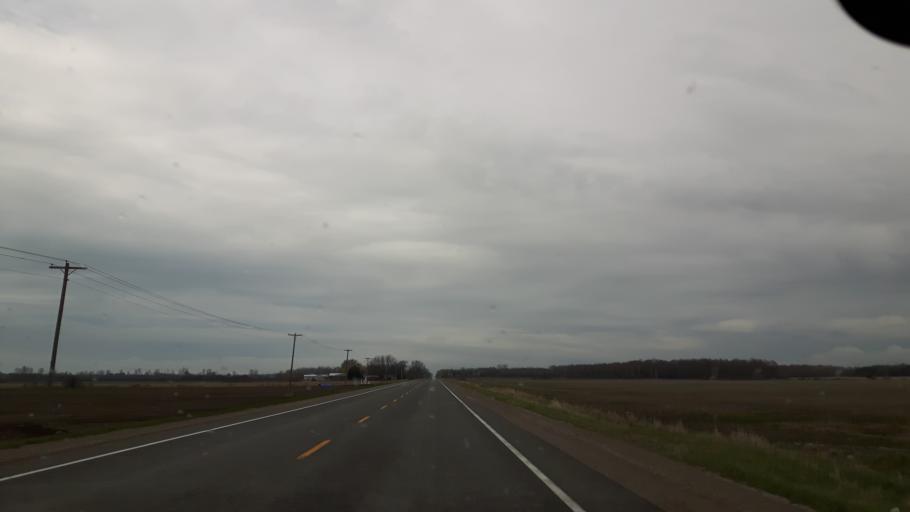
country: CA
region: Ontario
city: Goderich
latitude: 43.6367
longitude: -81.7057
